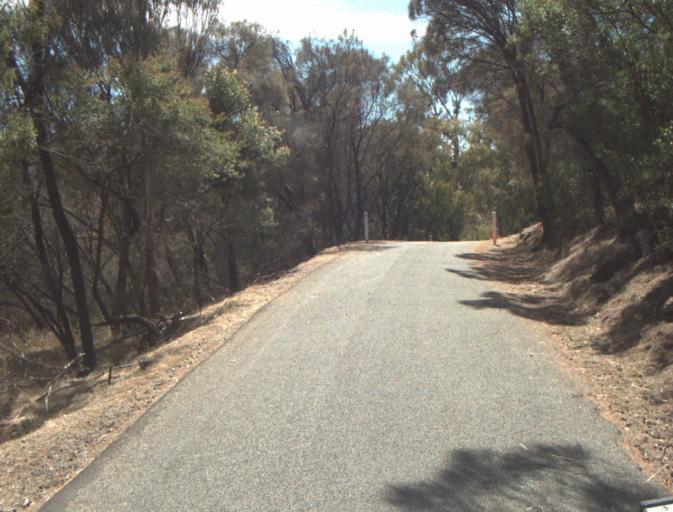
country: AU
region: Tasmania
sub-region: Launceston
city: Summerhill
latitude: -41.4594
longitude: 147.1138
